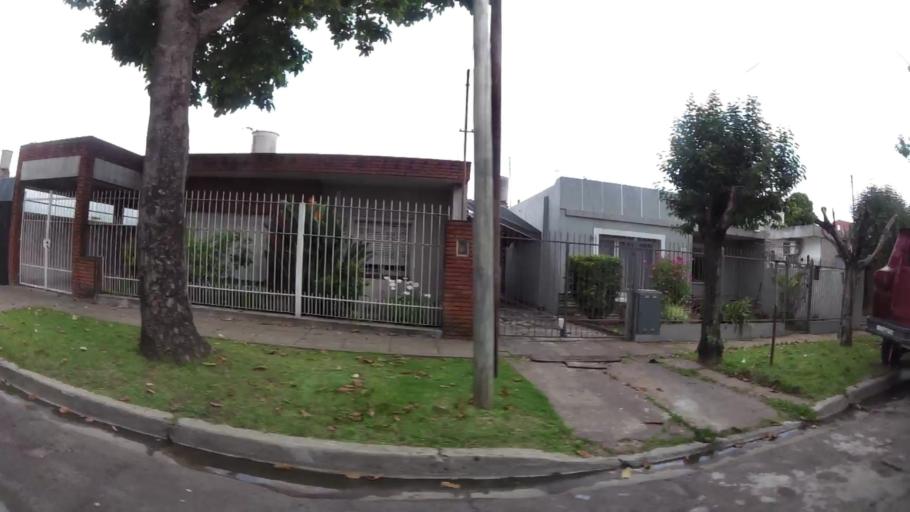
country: AR
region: Buenos Aires
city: Ituzaingo
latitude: -34.6383
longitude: -58.6883
